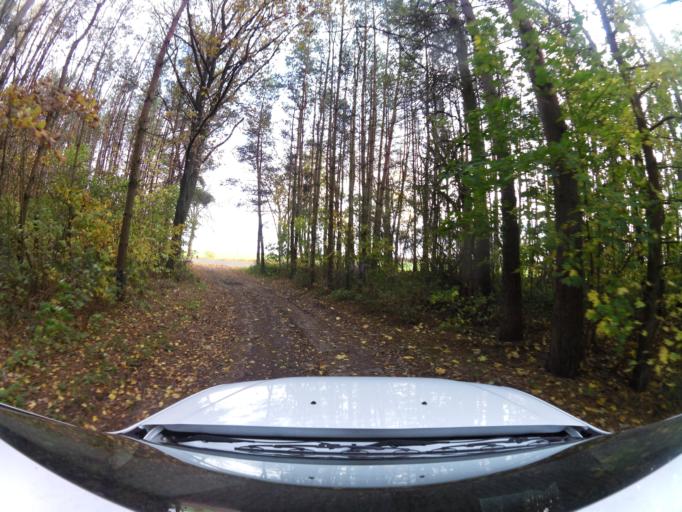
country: PL
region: West Pomeranian Voivodeship
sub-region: Powiat gryficki
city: Gryfice
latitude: 53.8713
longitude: 15.1210
